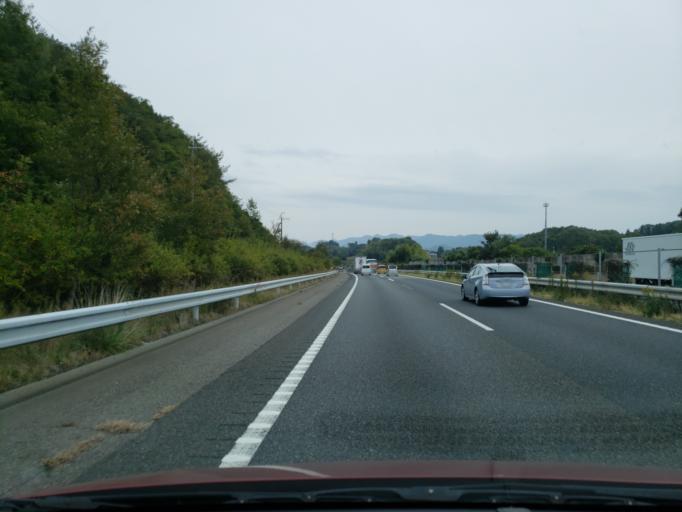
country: JP
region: Hyogo
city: Sandacho
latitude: 34.8283
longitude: 135.1717
